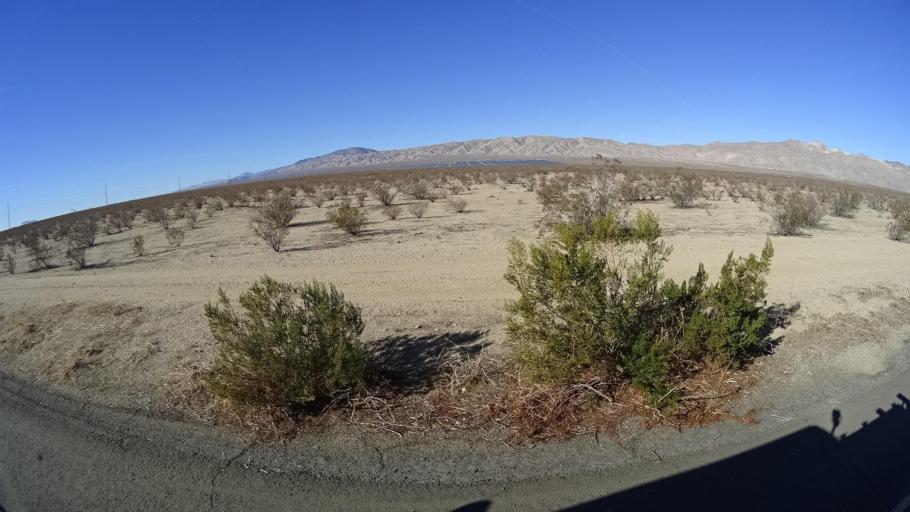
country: US
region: California
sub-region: Kern County
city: California City
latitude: 35.2032
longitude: -118.0213
